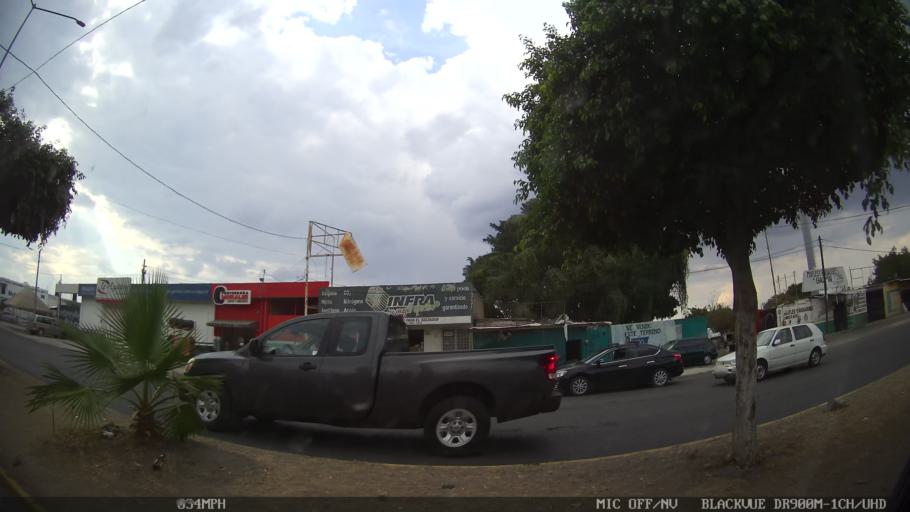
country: MX
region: Jalisco
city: Tlaquepaque
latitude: 20.6169
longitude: -103.2752
